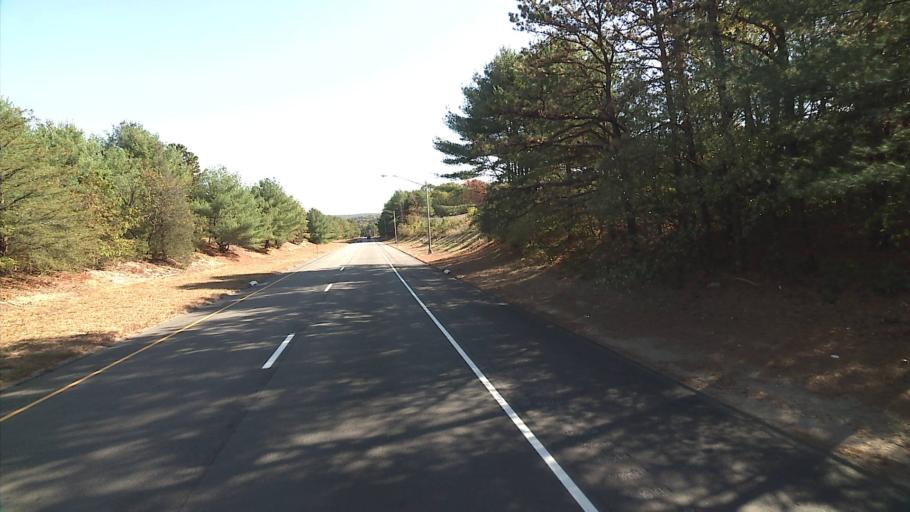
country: US
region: Connecticut
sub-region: Windham County
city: Willimantic
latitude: 41.7303
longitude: -72.2112
